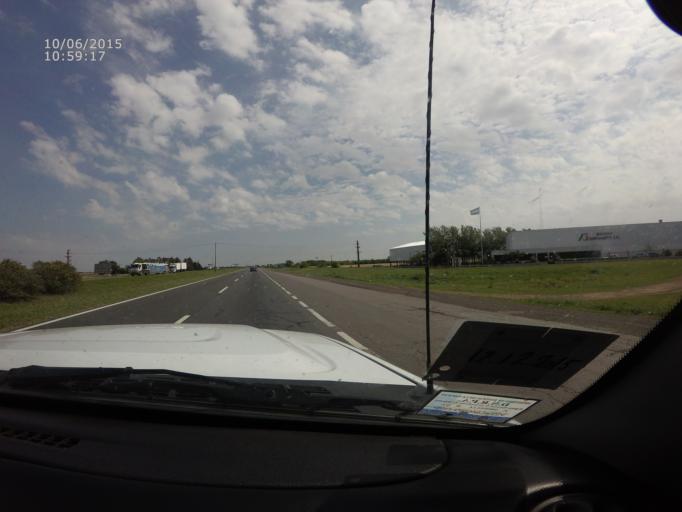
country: AR
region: Santa Fe
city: Villa Constitucion
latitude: -33.2845
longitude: -60.3825
